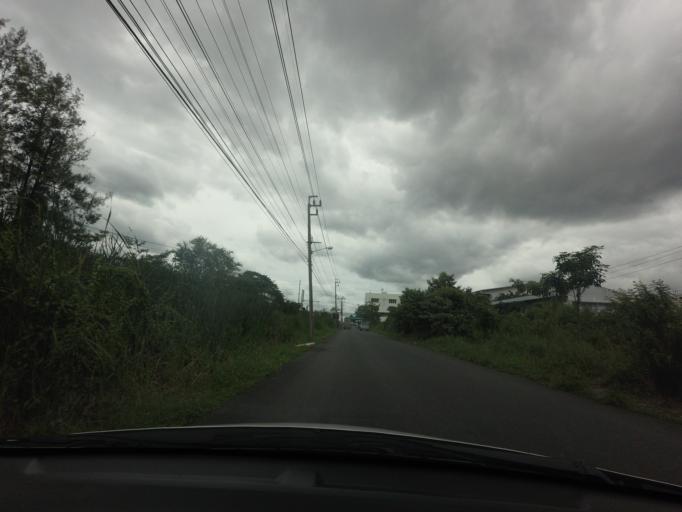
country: TH
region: Bangkok
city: Min Buri
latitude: 13.7753
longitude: 100.7477
